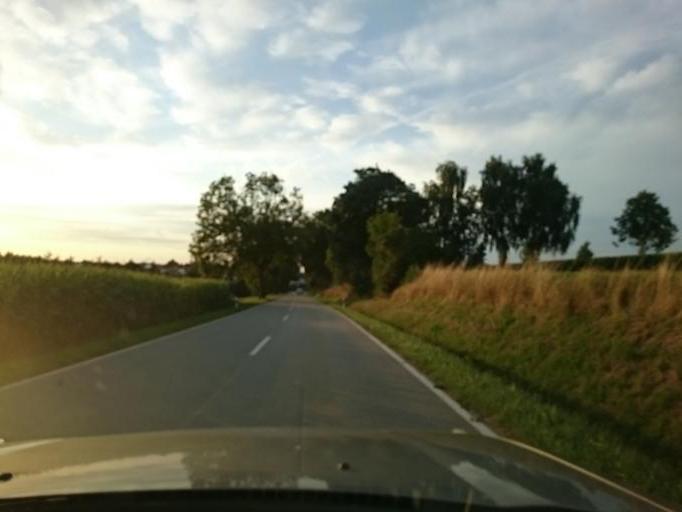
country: DE
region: Bavaria
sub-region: Lower Bavaria
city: Oberschneiding
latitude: 48.7900
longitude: 12.6470
